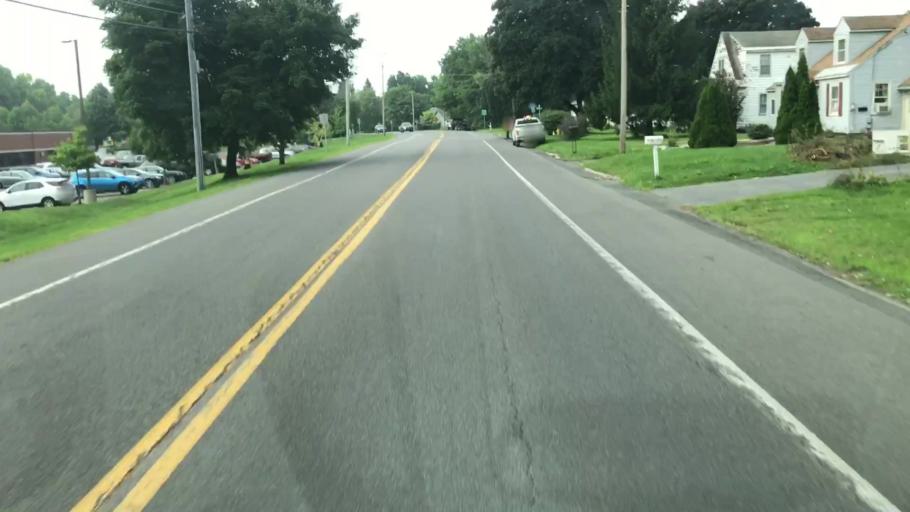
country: US
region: New York
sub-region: Onondaga County
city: Galeville
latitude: 43.0842
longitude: -76.1763
